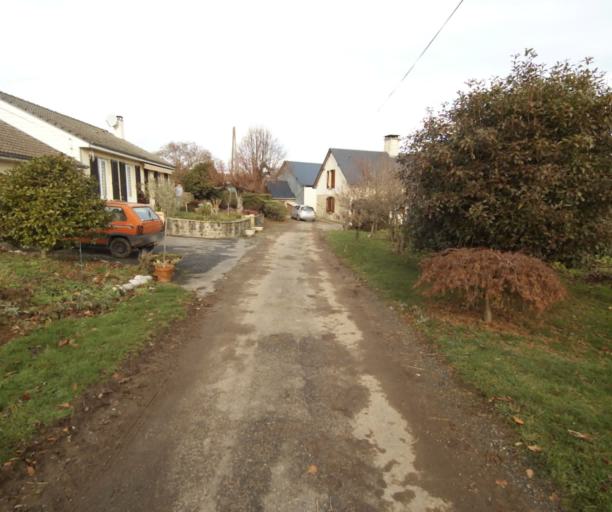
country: FR
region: Limousin
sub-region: Departement de la Correze
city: Chameyrat
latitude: 45.2523
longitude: 1.6900
